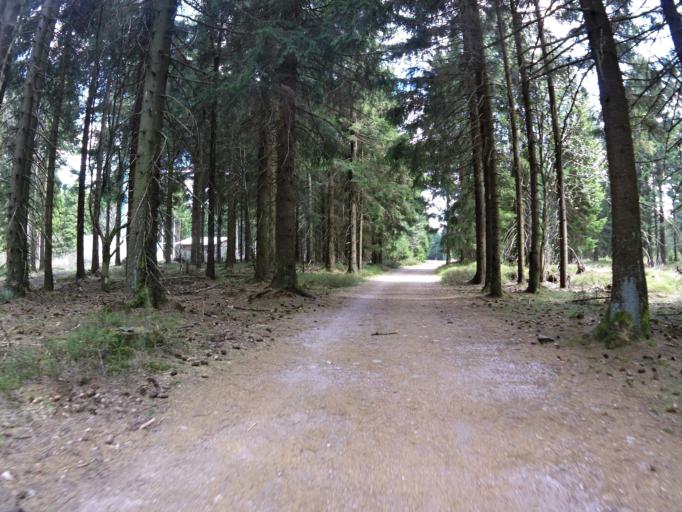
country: DE
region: Thuringia
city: Oberhof
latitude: 50.7021
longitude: 10.7054
